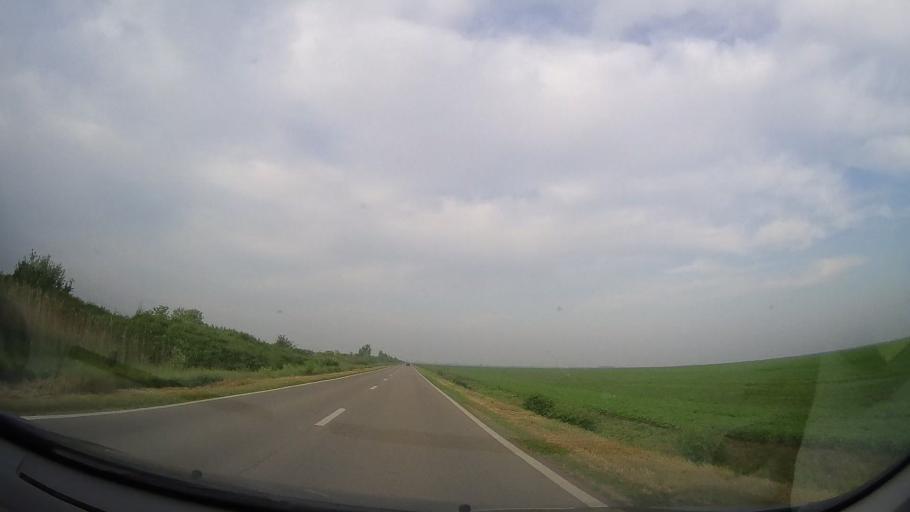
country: RO
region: Timis
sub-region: Comuna Parta
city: Parta
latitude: 45.6296
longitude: 21.0976
